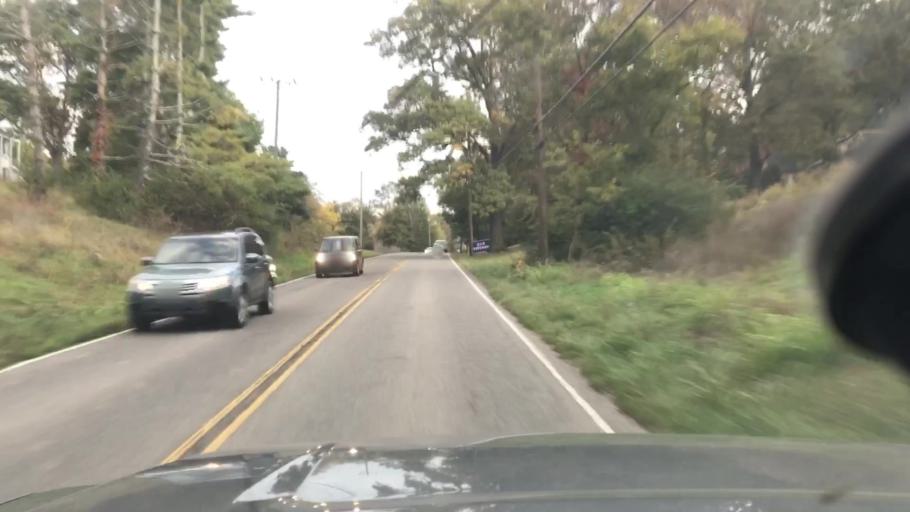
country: US
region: Tennessee
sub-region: Davidson County
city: Forest Hills
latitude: 36.0533
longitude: -86.8161
